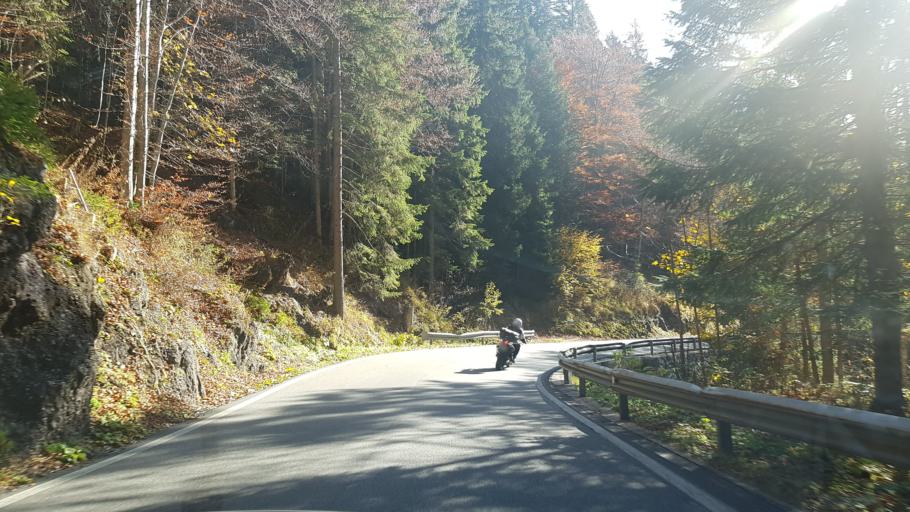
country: IT
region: Veneto
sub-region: Provincia di Belluno
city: Candide
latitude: 46.6442
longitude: 12.4529
